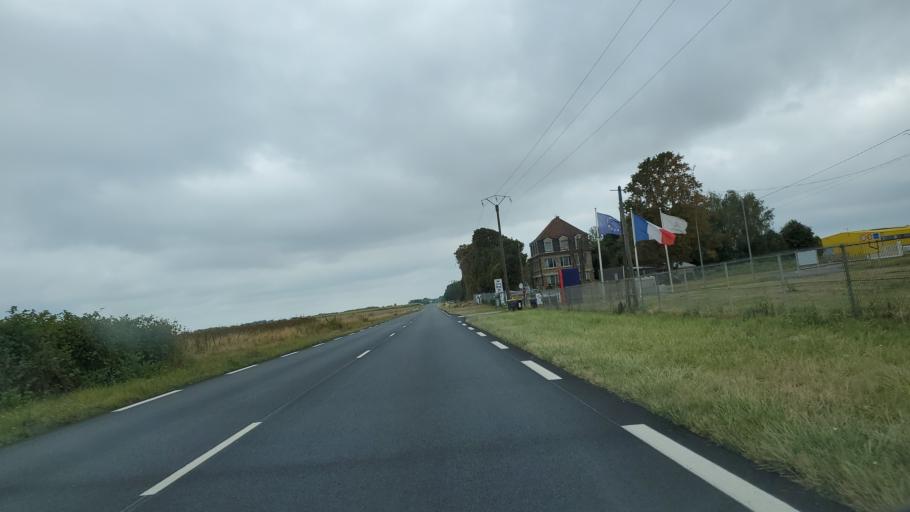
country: FR
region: Ile-de-France
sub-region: Departement de Seine-et-Marne
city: Pommeuse
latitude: 48.8317
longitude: 3.0111
